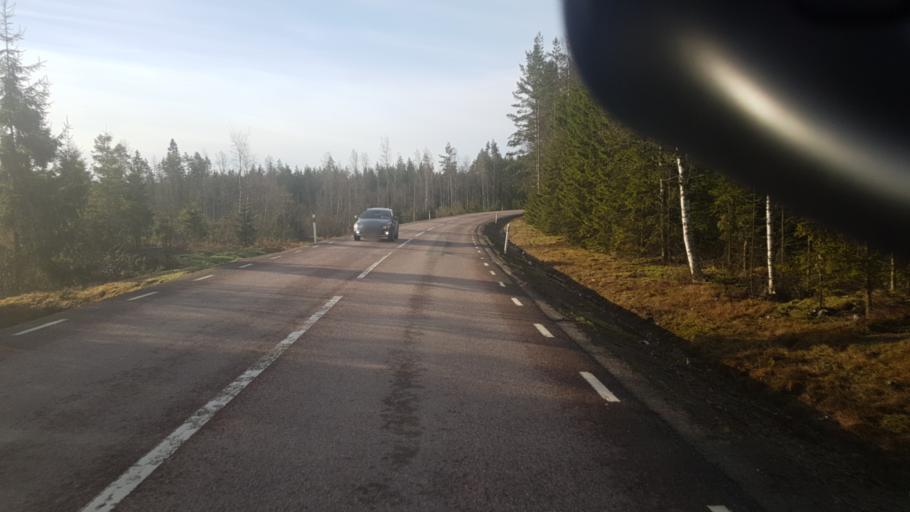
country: SE
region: Vaermland
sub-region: Eda Kommun
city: Charlottenberg
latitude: 59.8653
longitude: 12.2960
